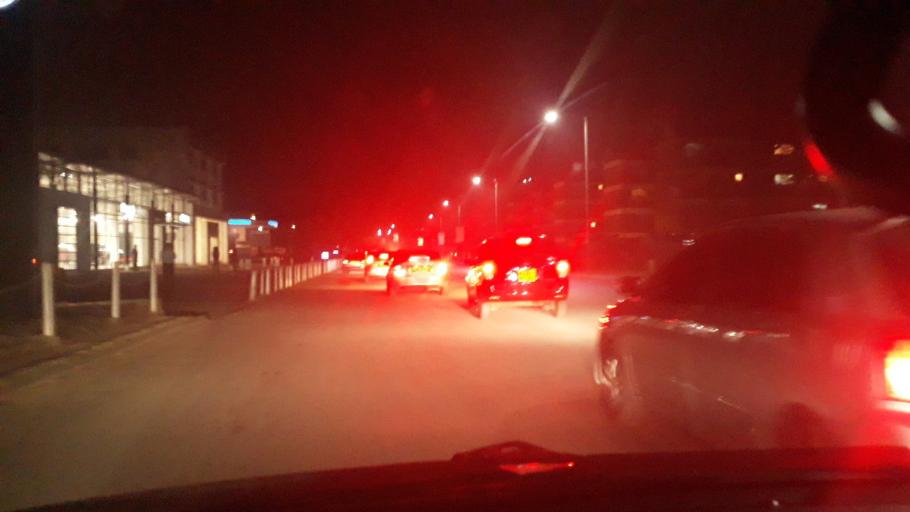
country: KE
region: Nairobi Area
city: Pumwani
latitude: -1.2979
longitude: 36.8360
